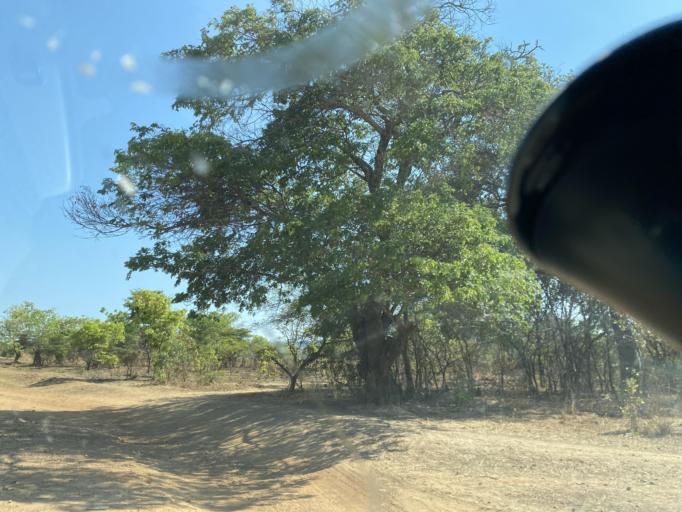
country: ZM
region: Lusaka
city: Chongwe
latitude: -15.2233
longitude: 28.8395
